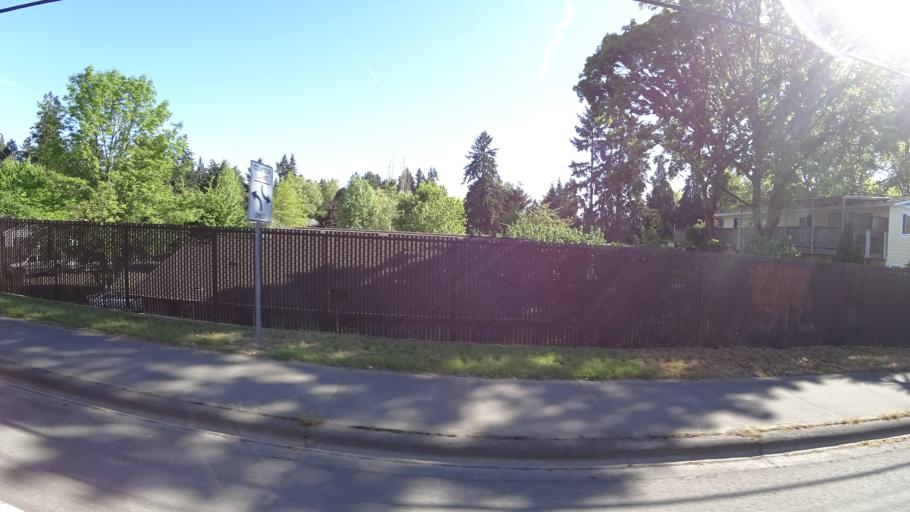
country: US
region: Oregon
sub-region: Washington County
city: Hillsboro
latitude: 45.5211
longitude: -122.9597
